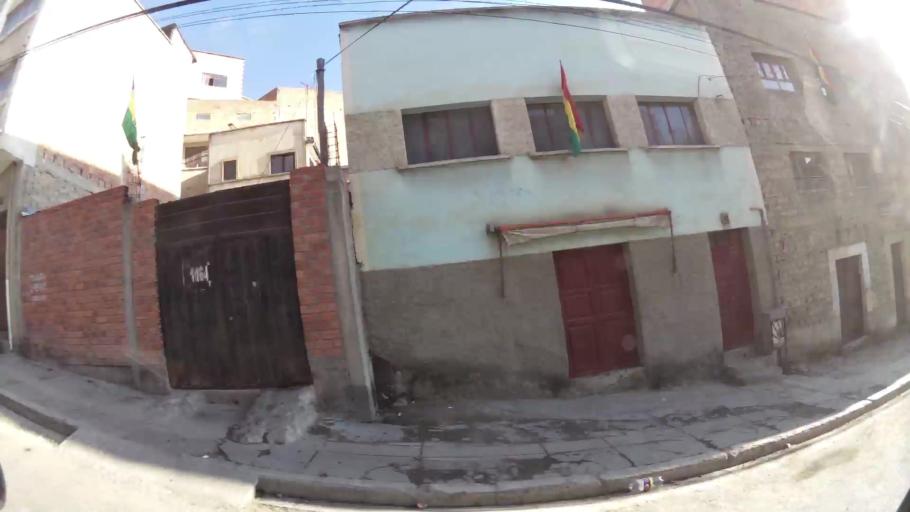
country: BO
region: La Paz
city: La Paz
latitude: -16.5020
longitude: -68.1474
